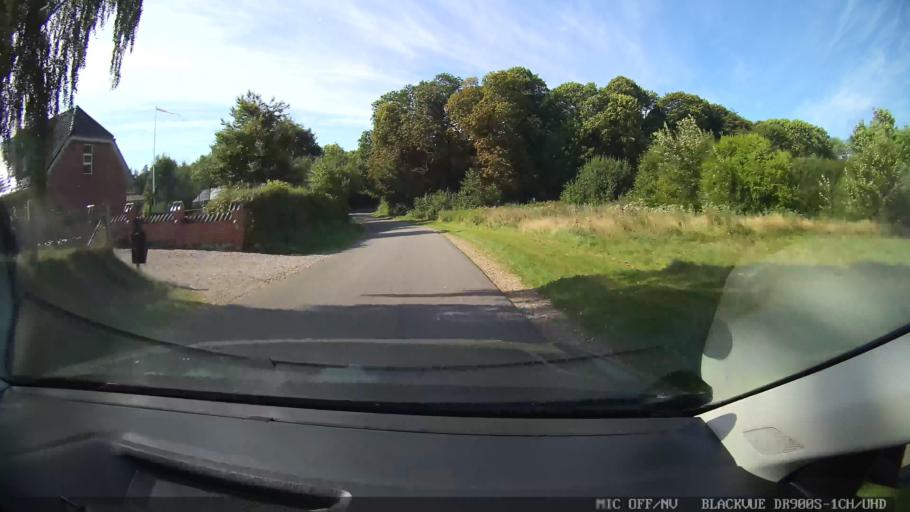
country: DK
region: North Denmark
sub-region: Mariagerfjord Kommune
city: Hobro
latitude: 56.5285
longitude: 9.7331
